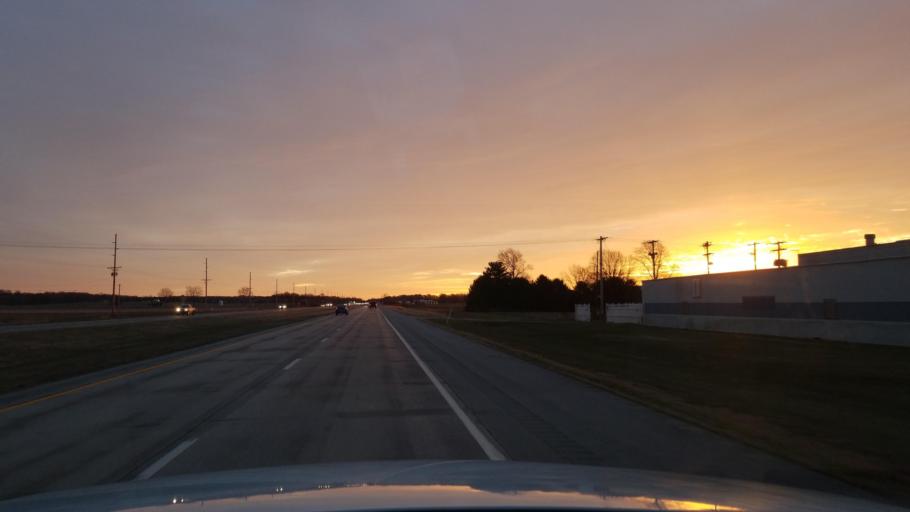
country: US
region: Indiana
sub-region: Posey County
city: Mount Vernon
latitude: 37.9421
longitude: -87.7842
